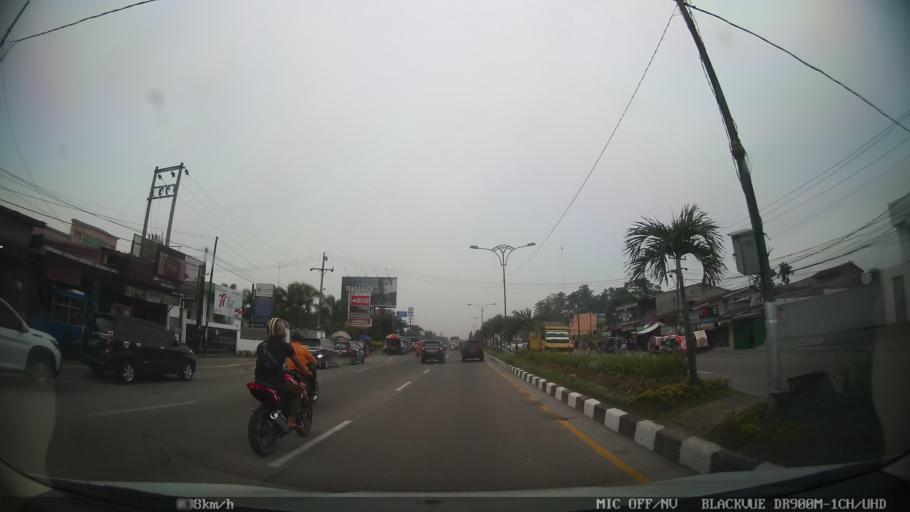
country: ID
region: North Sumatra
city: Deli Tua
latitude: 3.5374
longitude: 98.7107
